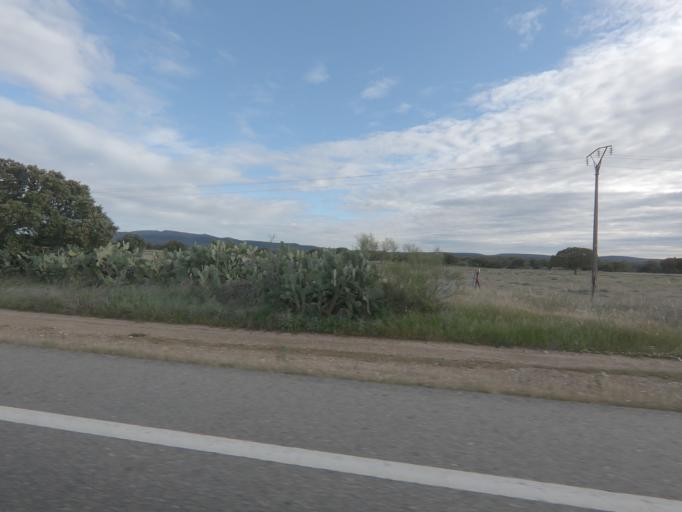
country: ES
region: Extremadura
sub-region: Provincia de Caceres
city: Torrejoncillo
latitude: 39.8826
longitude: -6.4611
